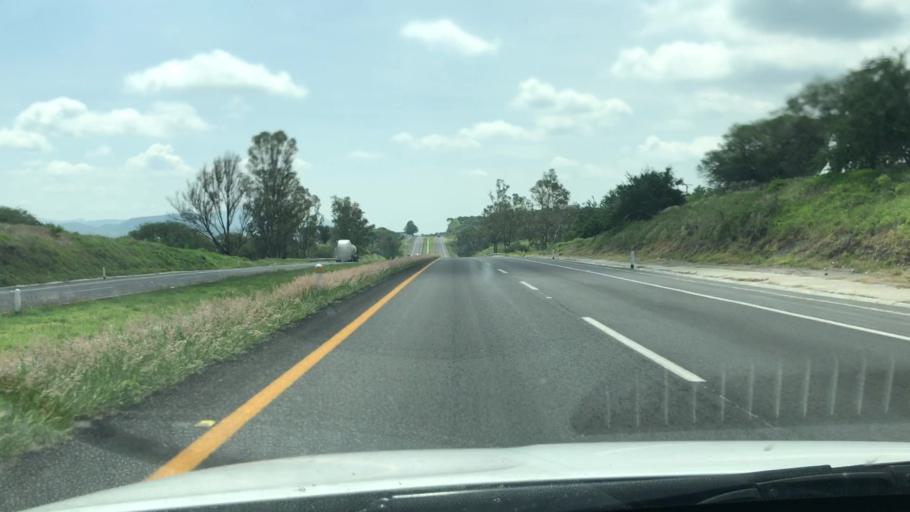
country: MX
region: Jalisco
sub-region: Poncitlan
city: Santa Cruz el Grande
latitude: 20.4372
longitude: -102.8054
